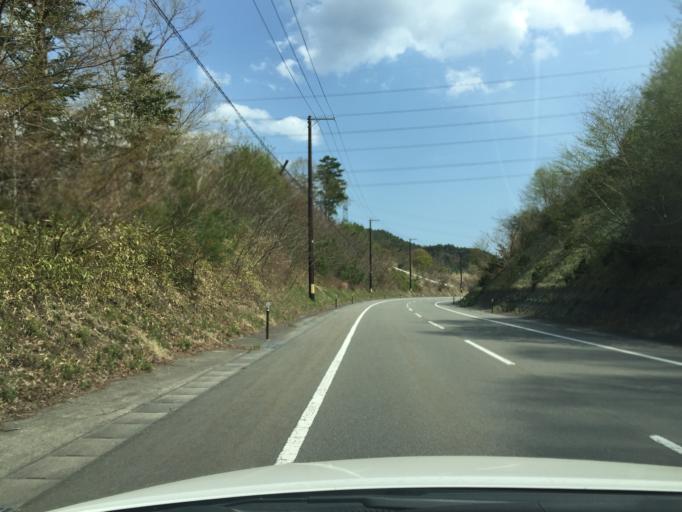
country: JP
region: Fukushima
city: Iwaki
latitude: 37.2869
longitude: 140.8413
